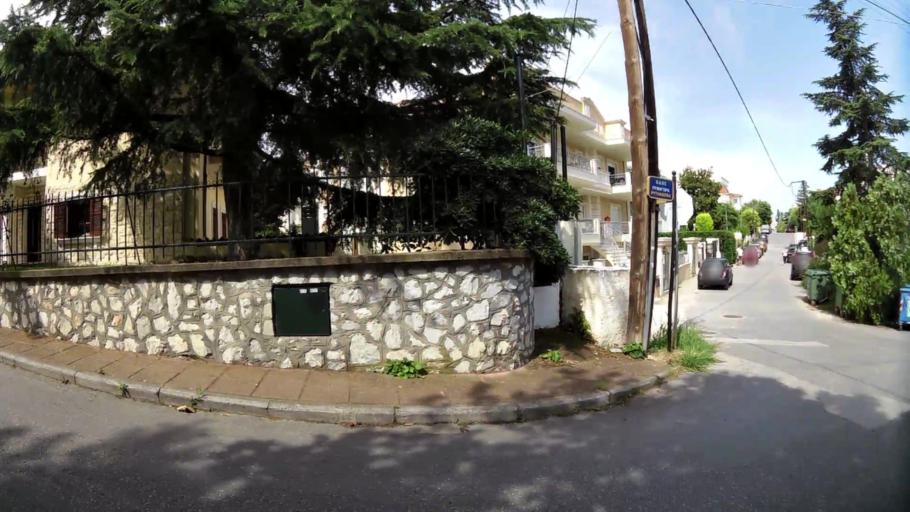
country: GR
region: Central Macedonia
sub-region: Nomos Thessalonikis
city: Panorama
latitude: 40.5797
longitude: 23.0133
